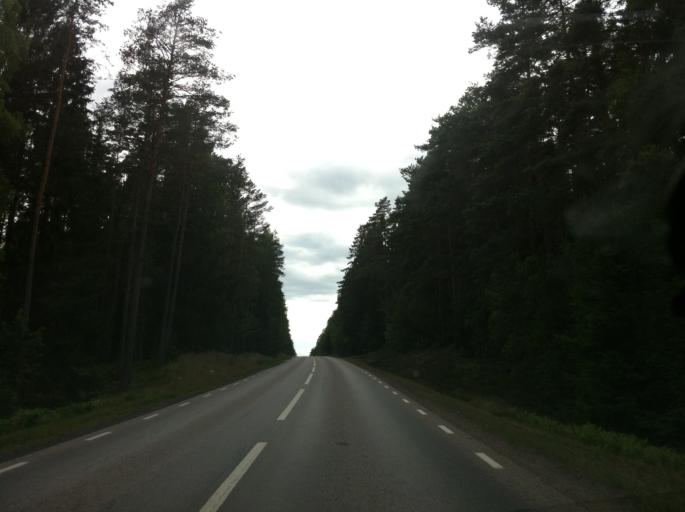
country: SE
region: Kronoberg
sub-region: Lessebo Kommun
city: Lessebo
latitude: 56.5552
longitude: 15.3174
